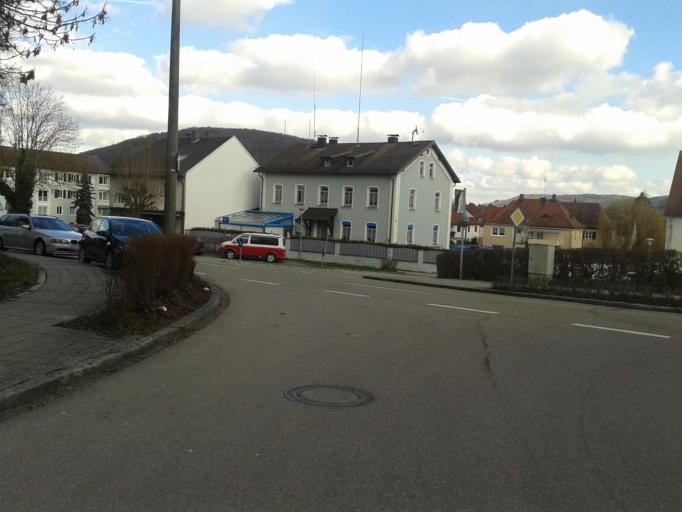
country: DE
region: Bavaria
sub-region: Regierungsbezirk Mittelfranken
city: Treuchtlingen
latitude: 48.9613
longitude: 10.9091
